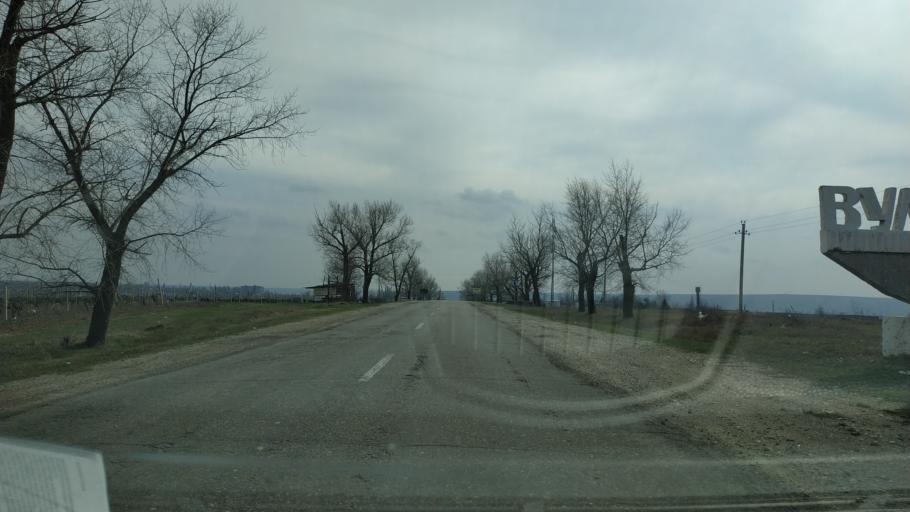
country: MD
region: Gagauzia
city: Vulcanesti
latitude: 45.7026
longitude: 28.4018
